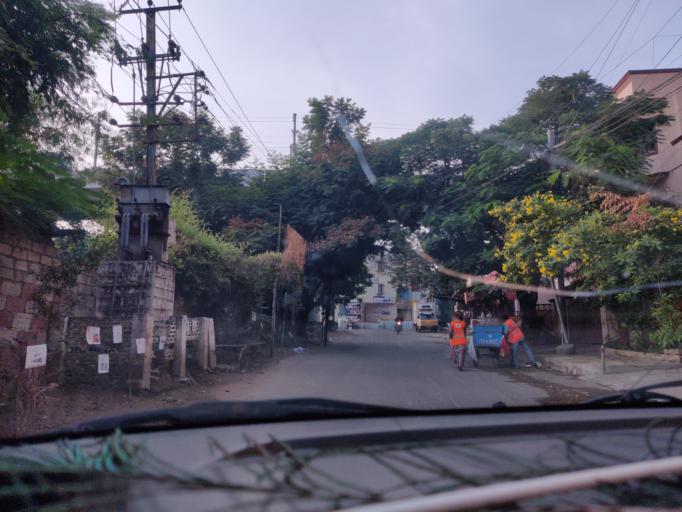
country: IN
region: Telangana
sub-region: Rangareddi
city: Kukatpalli
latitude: 17.4382
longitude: 78.4404
